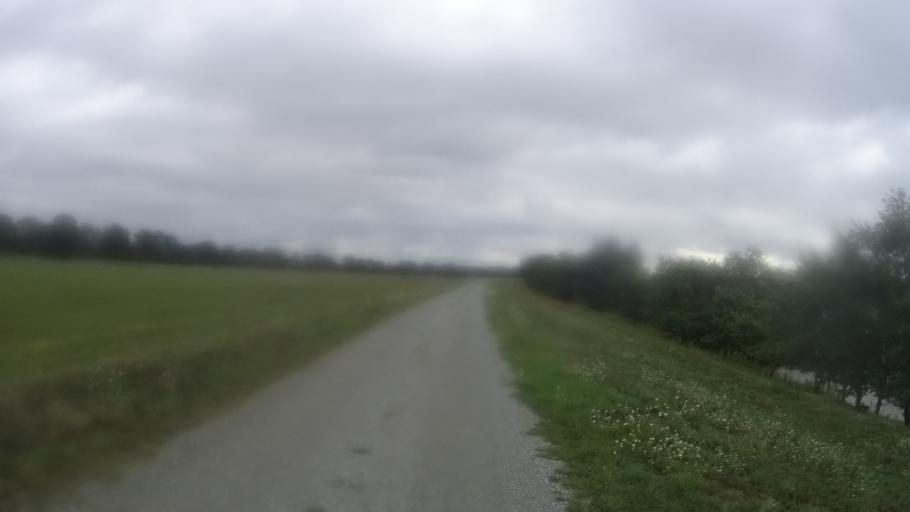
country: DE
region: Lower Saxony
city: Gorleben
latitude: 53.0569
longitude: 11.3542
